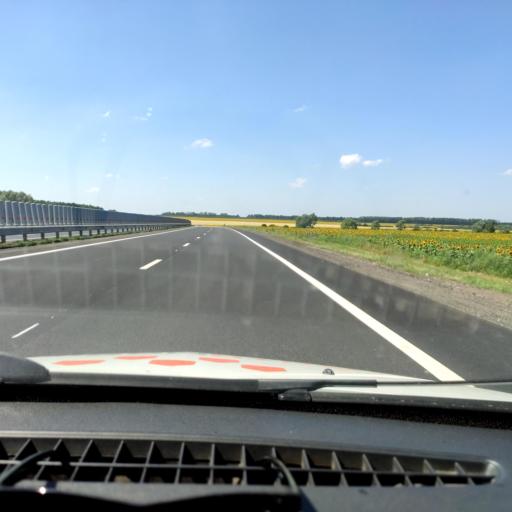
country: RU
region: Bashkortostan
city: Kushnarenkovo
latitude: 55.0674
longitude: 55.3553
